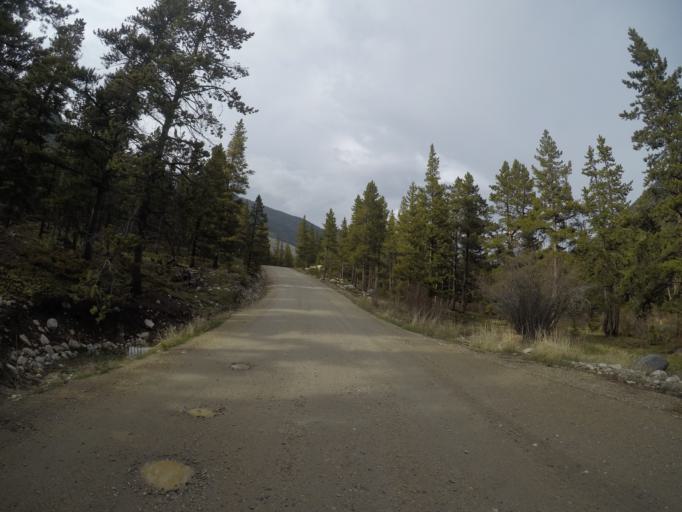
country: US
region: Montana
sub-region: Carbon County
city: Red Lodge
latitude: 45.0467
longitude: -109.4246
